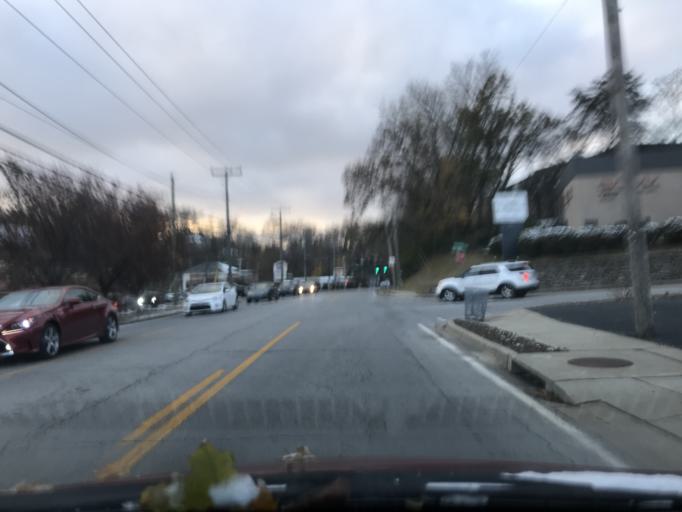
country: US
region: Indiana
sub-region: Clark County
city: Jeffersonville
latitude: 38.2585
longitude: -85.7030
